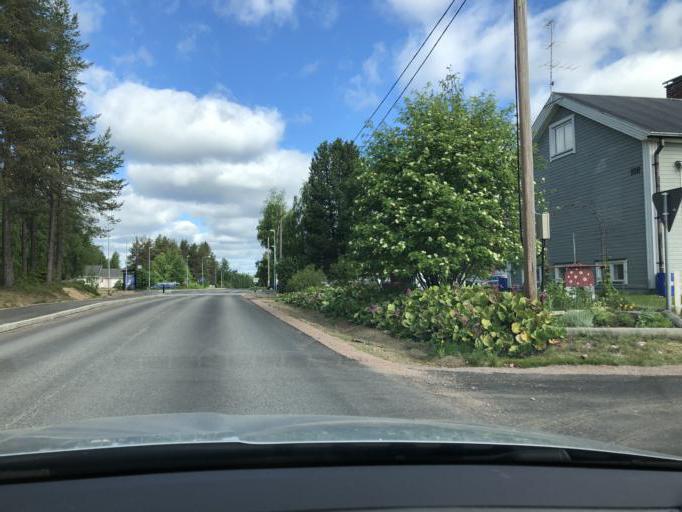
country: SE
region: Norrbotten
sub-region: Pajala Kommun
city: Pajala
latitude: 67.2224
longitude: 23.3443
